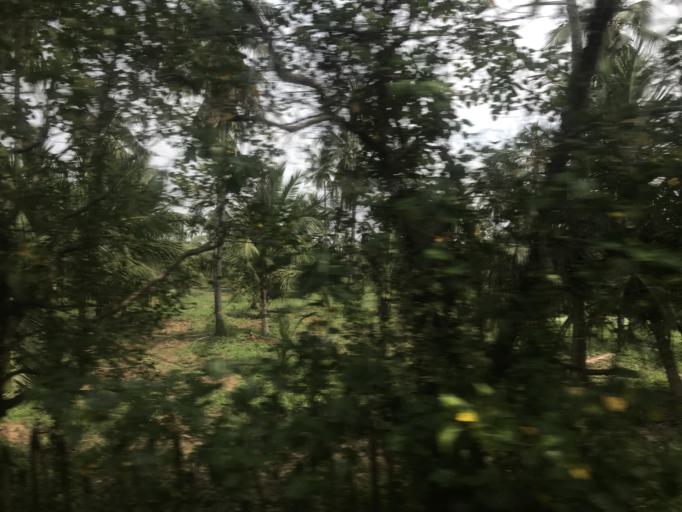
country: LK
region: Northern Province
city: Kilinochchi
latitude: 9.5925
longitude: 80.3450
